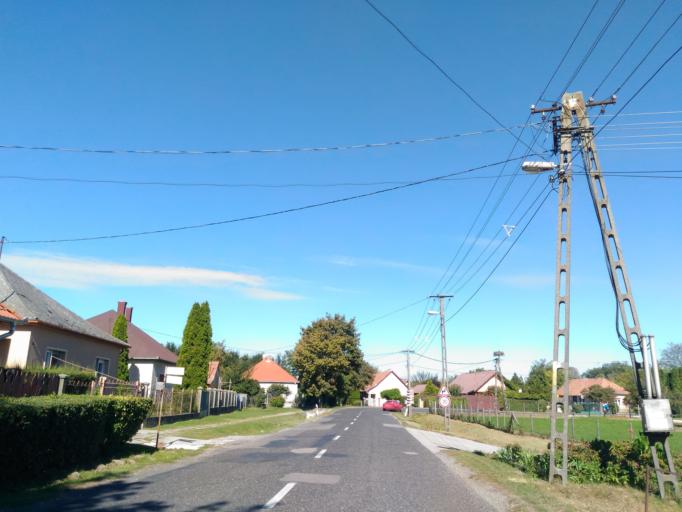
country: HU
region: Fejer
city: Ivancsa
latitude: 47.1424
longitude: 18.8343
